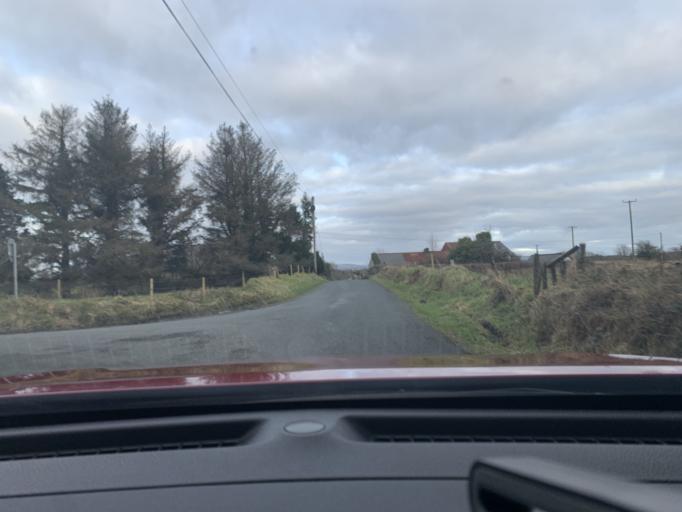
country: IE
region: Connaught
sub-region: Roscommon
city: Ballaghaderreen
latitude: 53.9781
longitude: -8.5576
